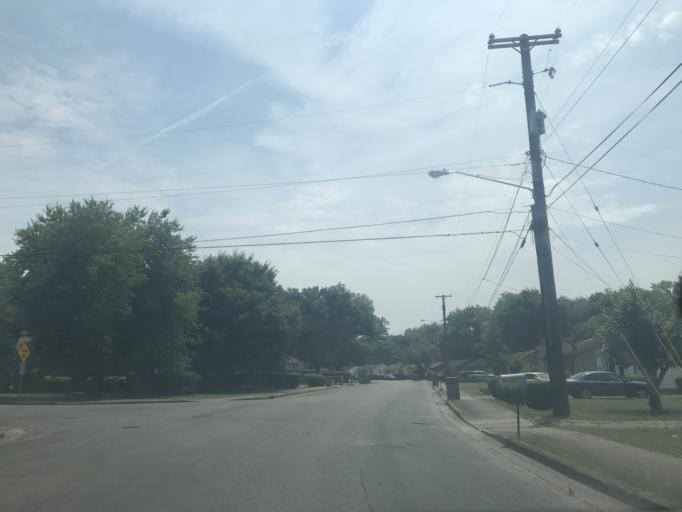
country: US
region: Tennessee
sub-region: Davidson County
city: Nashville
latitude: 36.1851
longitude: -86.8224
